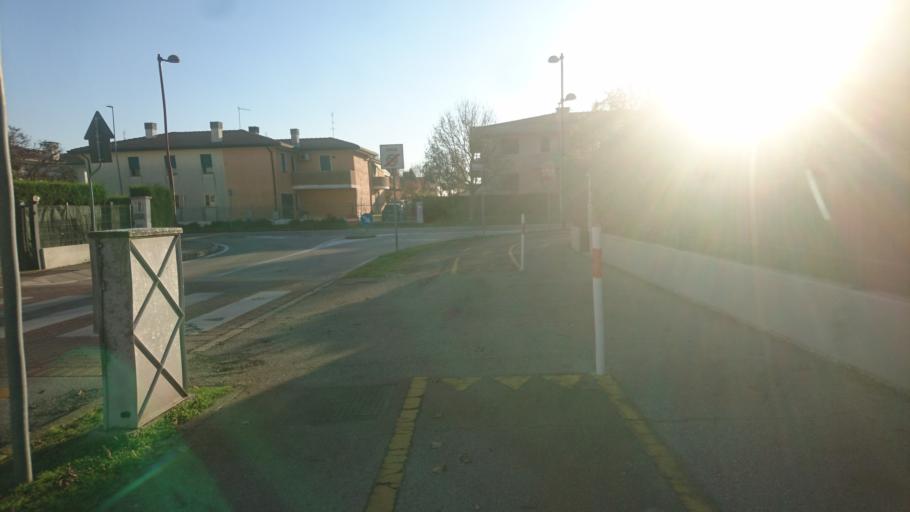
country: IT
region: Veneto
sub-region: Provincia di Padova
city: Villaguattera
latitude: 45.4469
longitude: 11.8149
